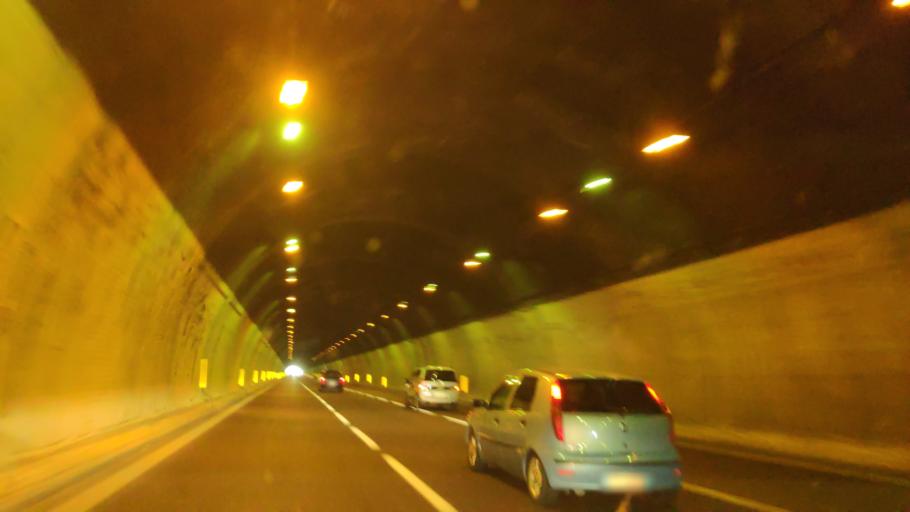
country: IT
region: Campania
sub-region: Provincia di Salerno
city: Lanzara
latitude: 40.7732
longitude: 14.6574
